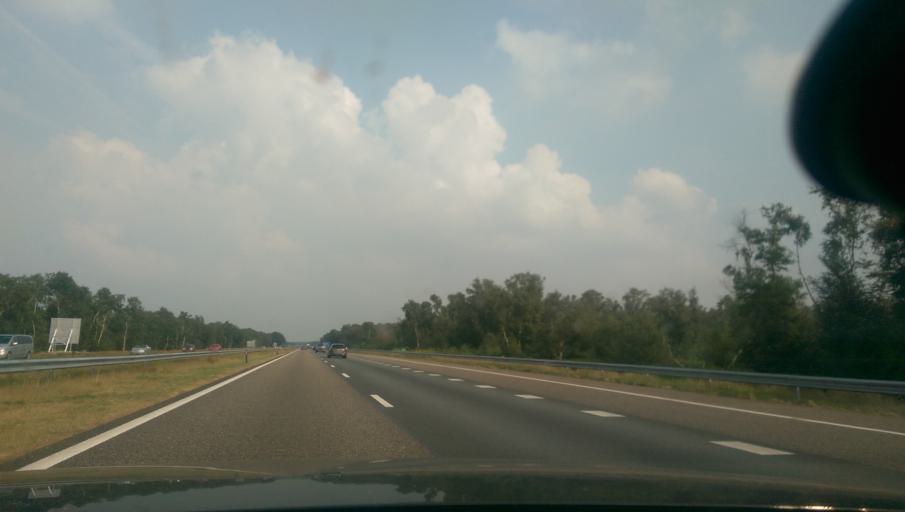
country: NL
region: North Brabant
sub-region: Gemeente Asten
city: Asten
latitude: 51.3891
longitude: 5.8721
